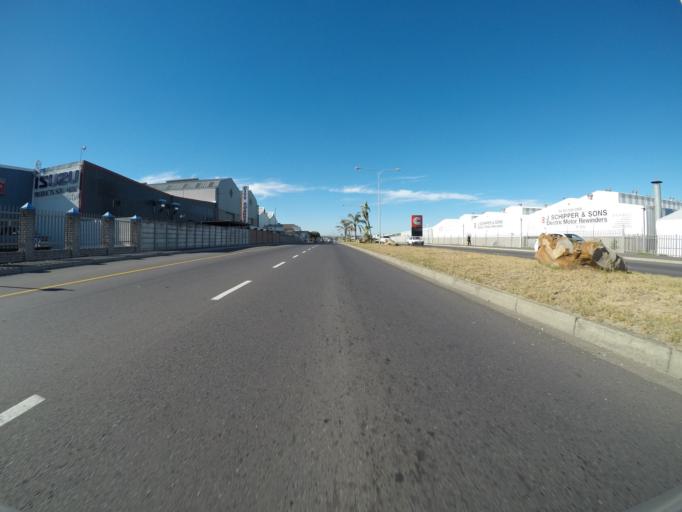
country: ZA
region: Western Cape
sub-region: City of Cape Town
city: Kraaifontein
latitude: -33.9011
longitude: 18.6696
